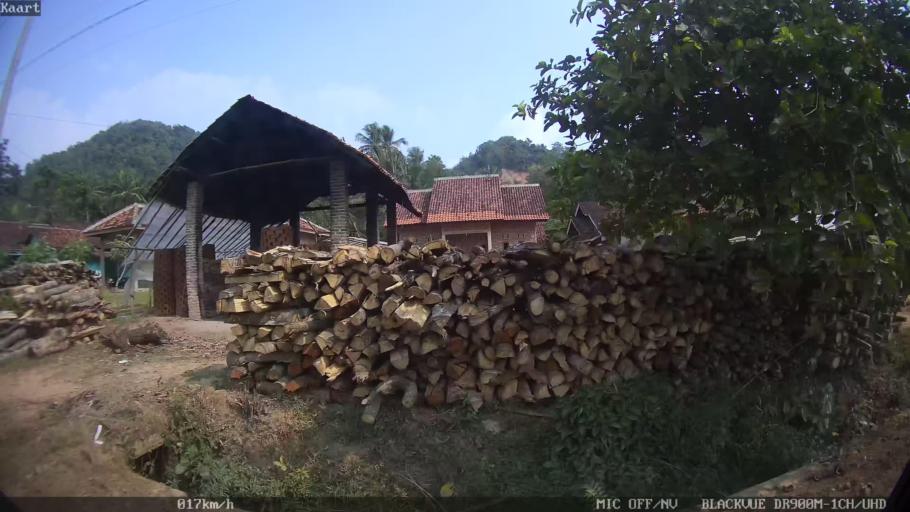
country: ID
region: Lampung
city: Pringsewu
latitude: -5.3819
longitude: 104.9994
